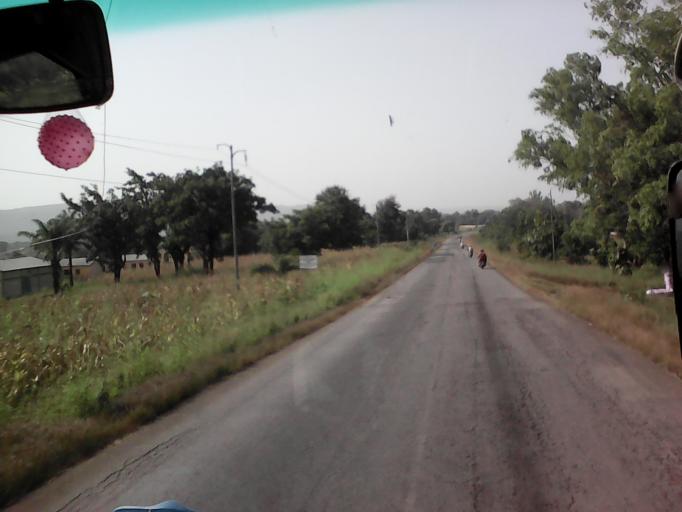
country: TG
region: Centrale
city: Sokode
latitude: 9.1075
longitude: 1.1439
